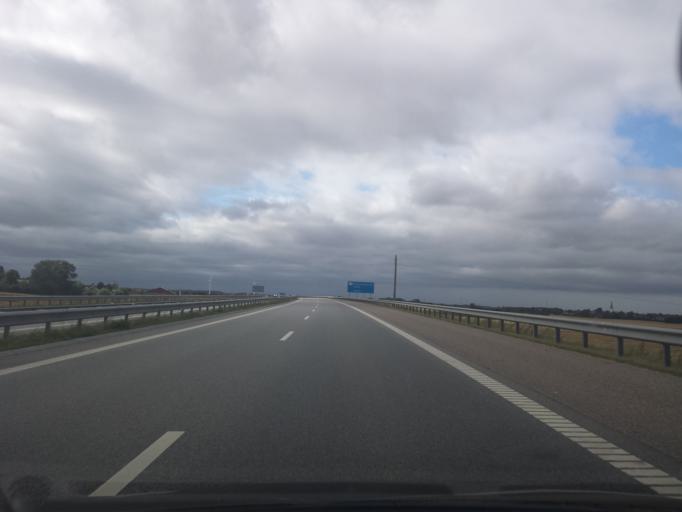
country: DK
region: South Denmark
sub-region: Sonderborg Kommune
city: Dybbol
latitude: 54.9297
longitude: 9.7114
